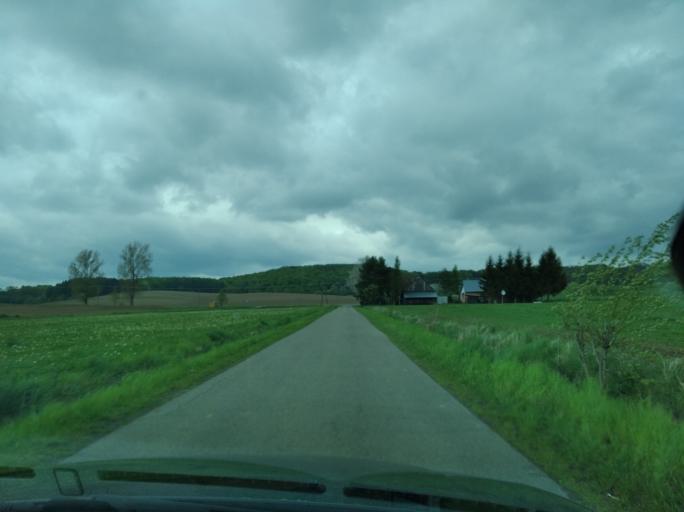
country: PL
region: Subcarpathian Voivodeship
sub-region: Powiat brzozowski
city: Turze Pole
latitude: 49.6272
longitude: 22.0075
